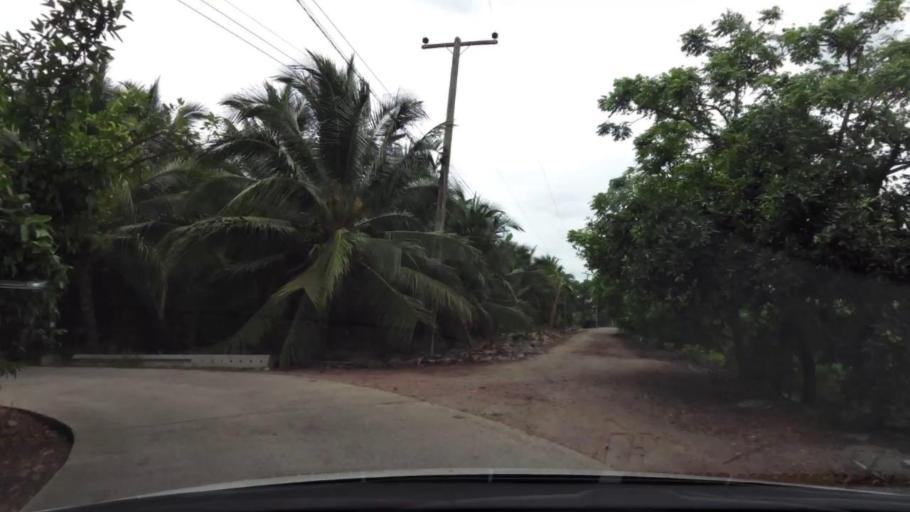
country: TH
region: Ratchaburi
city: Damnoen Saduak
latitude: 13.5604
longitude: 100.0073
